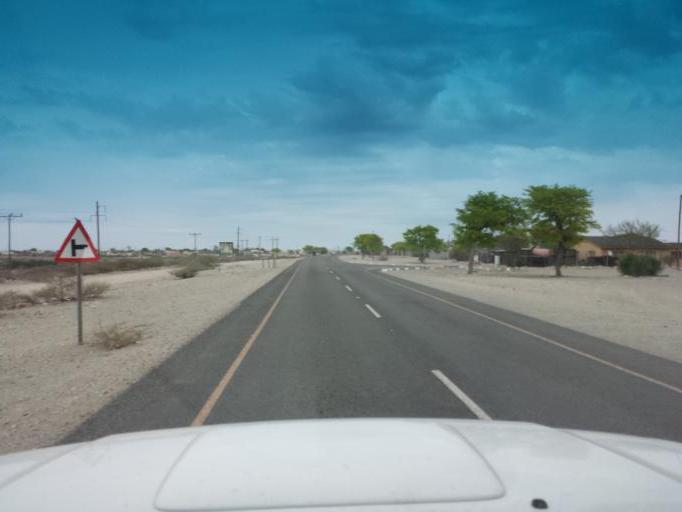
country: BW
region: Central
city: Mopipi
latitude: -21.2043
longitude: 24.8643
